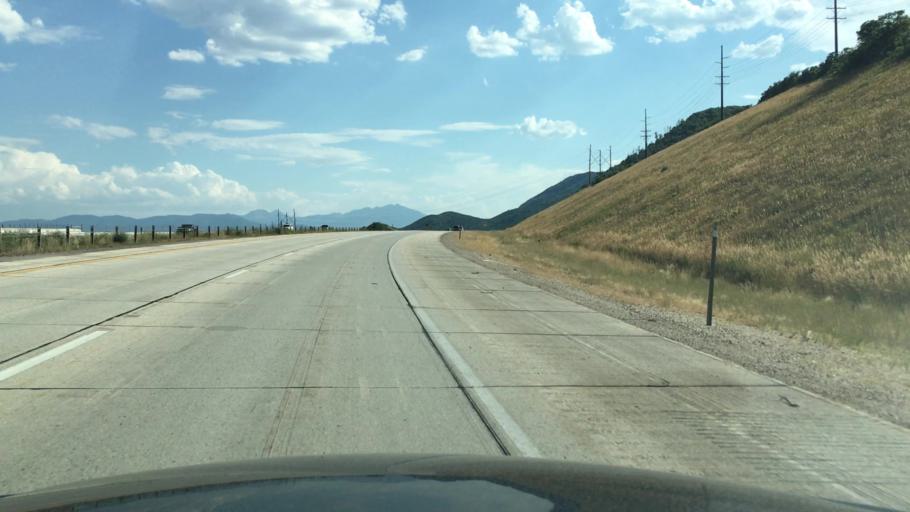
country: US
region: Utah
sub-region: Summit County
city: Park City
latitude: 40.6044
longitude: -111.4294
